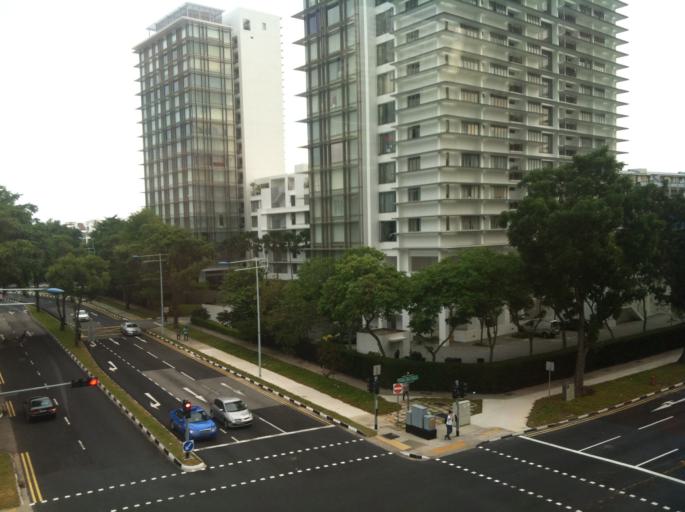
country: SG
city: Singapore
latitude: 1.3211
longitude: 103.9138
